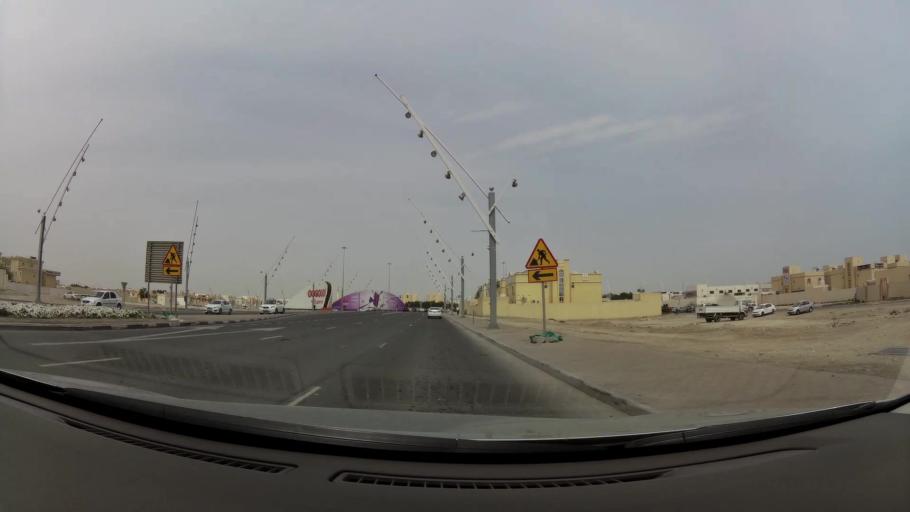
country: QA
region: Baladiyat ad Dawhah
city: Doha
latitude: 25.2678
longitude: 51.4768
